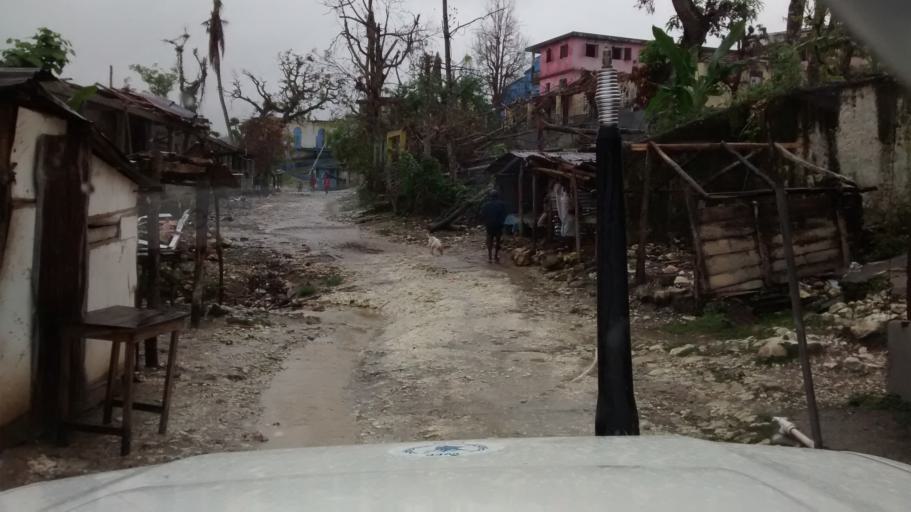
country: HT
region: Grandans
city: Moron
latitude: 18.5368
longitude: -74.1574
